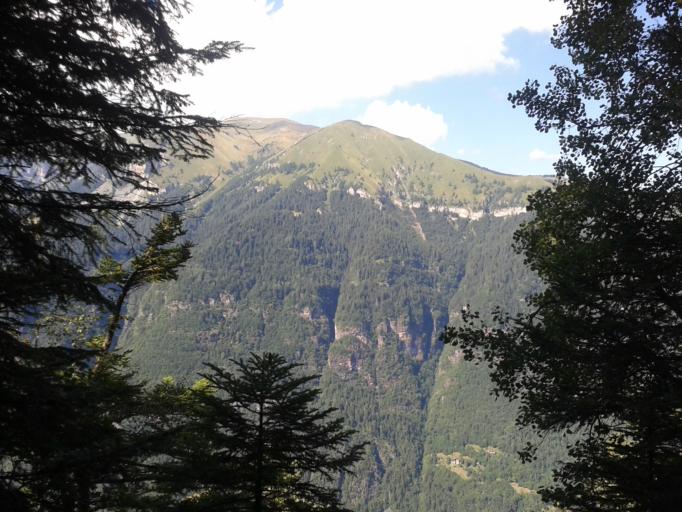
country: IT
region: Trentino-Alto Adige
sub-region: Provincia di Trento
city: Daone
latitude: 45.9418
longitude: 10.5933
